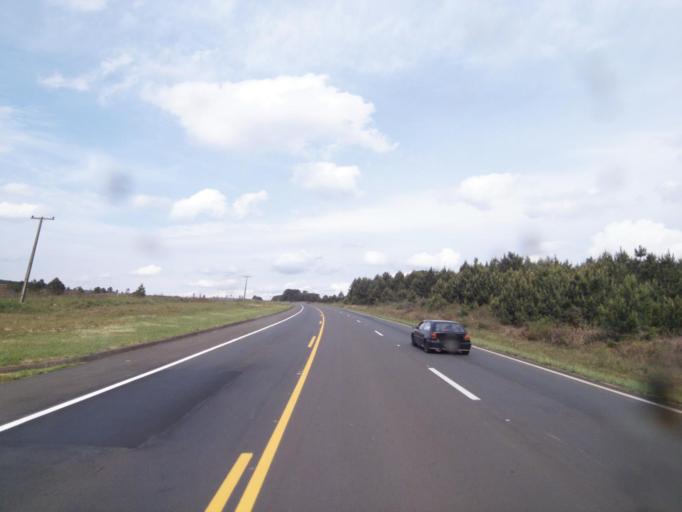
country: BR
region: Parana
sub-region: Campo Largo
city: Campo Largo
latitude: -25.4656
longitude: -49.7499
